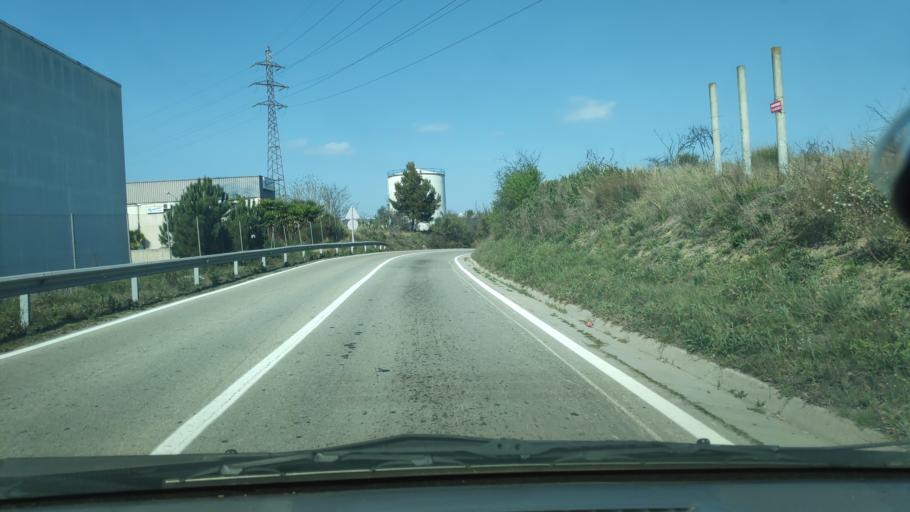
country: ES
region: Catalonia
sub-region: Provincia de Barcelona
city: Polinya
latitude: 41.5243
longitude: 2.1493
